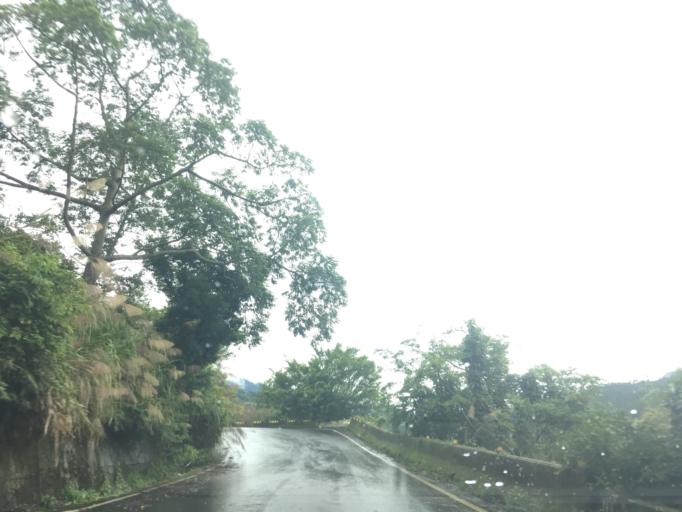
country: TW
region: Taiwan
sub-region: Yunlin
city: Douliu
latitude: 23.5583
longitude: 120.6573
